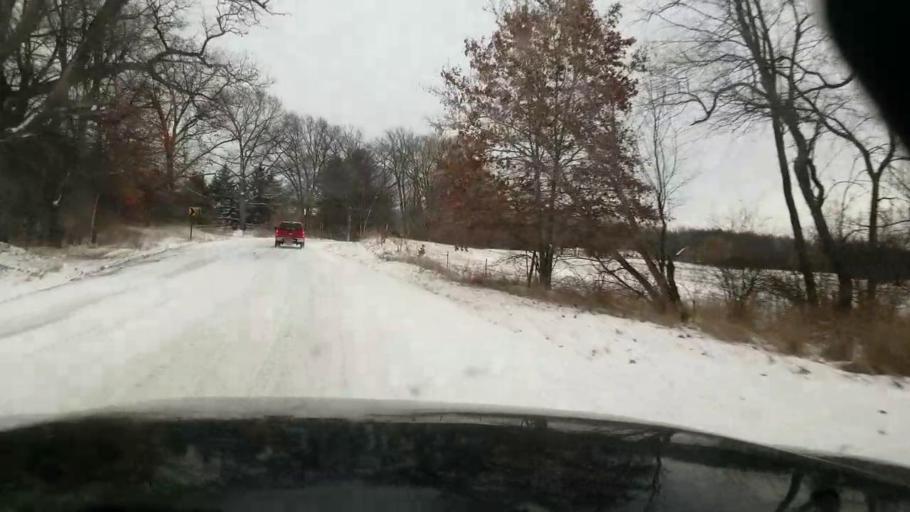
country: US
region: Michigan
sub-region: Jackson County
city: Spring Arbor
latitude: 42.1604
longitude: -84.5000
